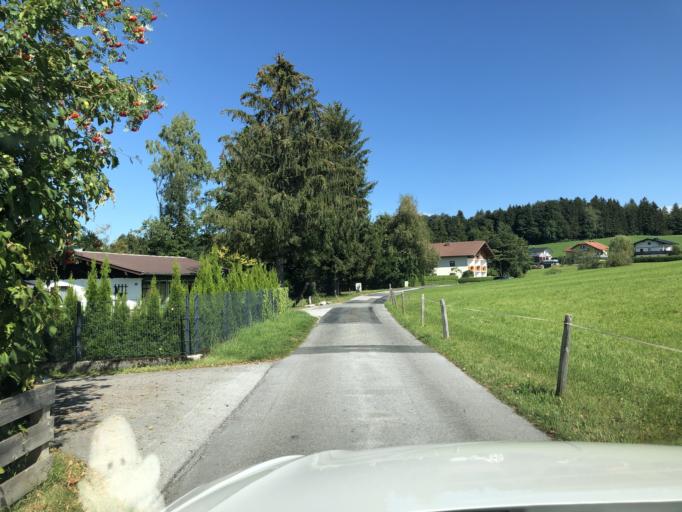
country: AT
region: Salzburg
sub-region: Politischer Bezirk Salzburg-Umgebung
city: Plainfeld
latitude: 47.8280
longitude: 13.1865
